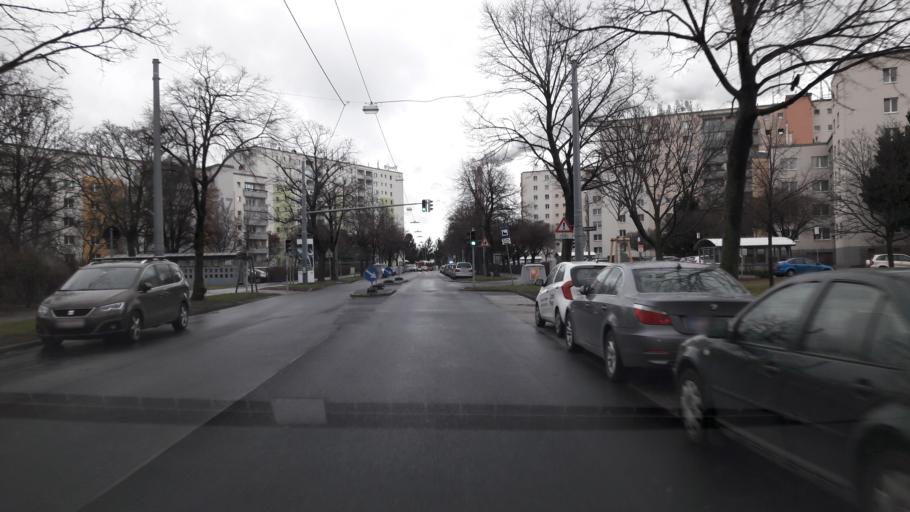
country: AT
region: Lower Austria
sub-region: Politischer Bezirk Wien-Umgebung
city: Schwechat
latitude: 48.1677
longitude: 16.4318
